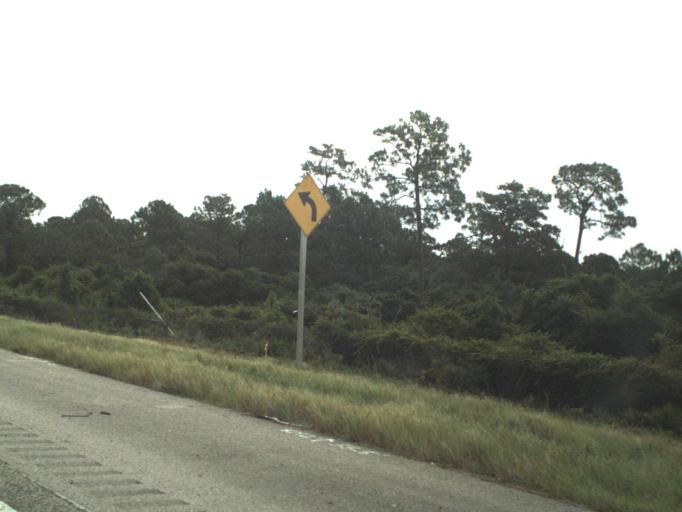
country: US
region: Florida
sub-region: Saint Lucie County
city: Fort Pierce South
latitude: 27.3993
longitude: -80.3903
